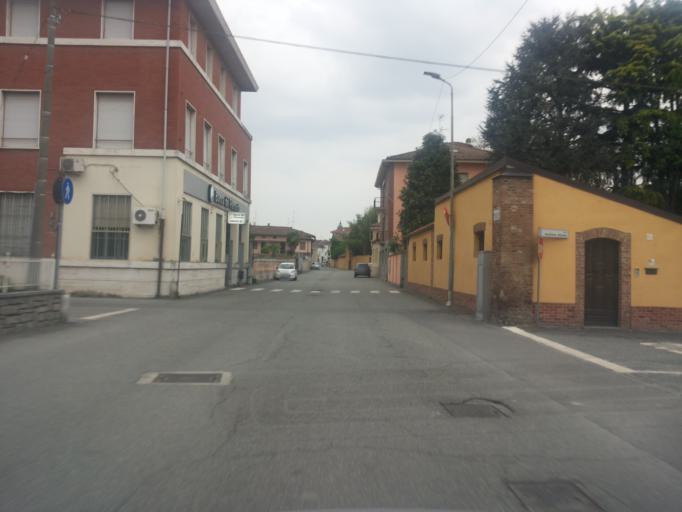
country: IT
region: Piedmont
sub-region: Provincia di Alessandria
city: Villanova Monferrato
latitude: 45.1801
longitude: 8.4805
